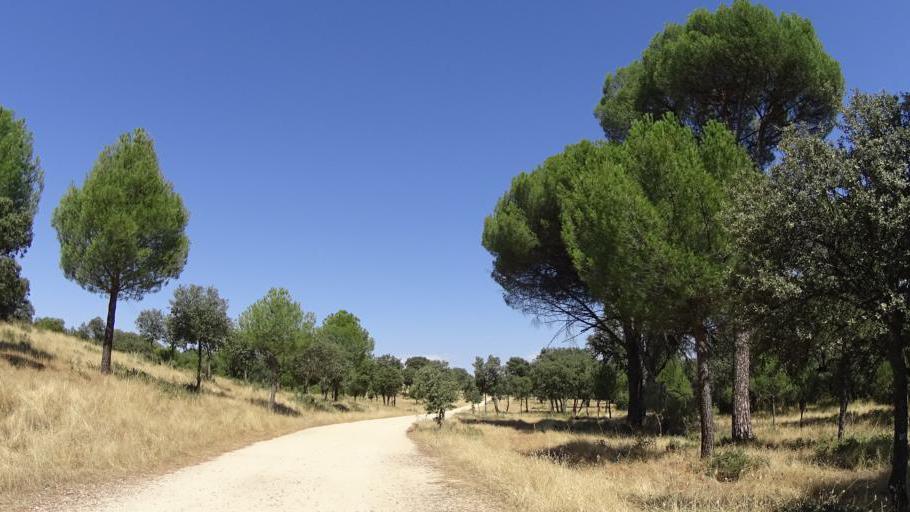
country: ES
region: Madrid
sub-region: Provincia de Madrid
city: Boadilla del Monte
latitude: 40.4286
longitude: -3.8546
